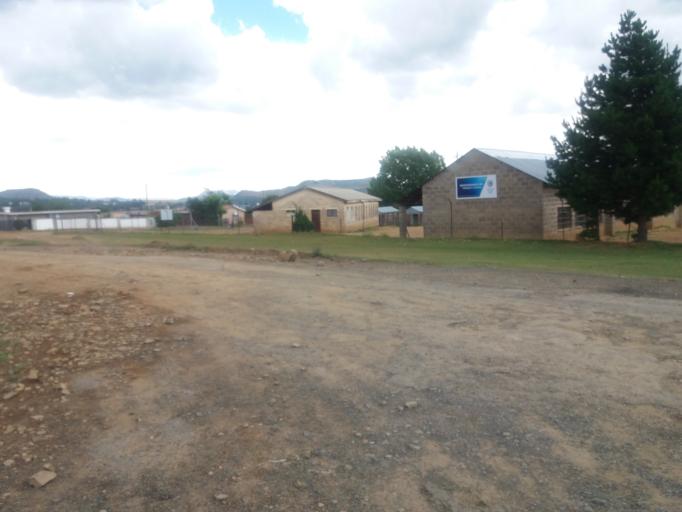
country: LS
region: Maseru
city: Maseru
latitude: -29.3001
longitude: 27.4979
